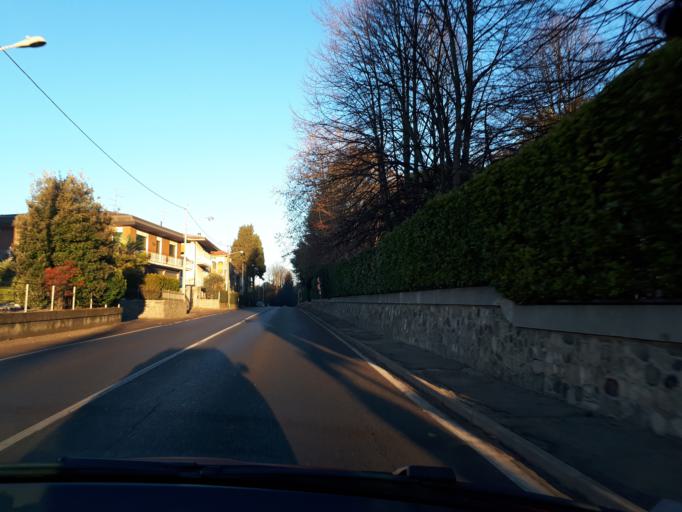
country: IT
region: Lombardy
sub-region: Provincia di Como
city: Fino Mornasco
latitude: 45.7382
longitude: 9.0544
